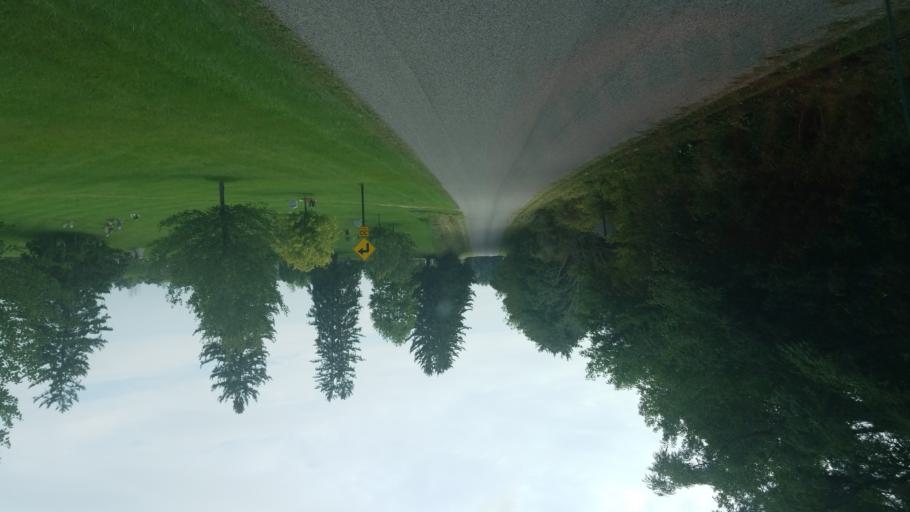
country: US
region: Ohio
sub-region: Wayne County
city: West Salem
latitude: 40.9295
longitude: -82.0531
